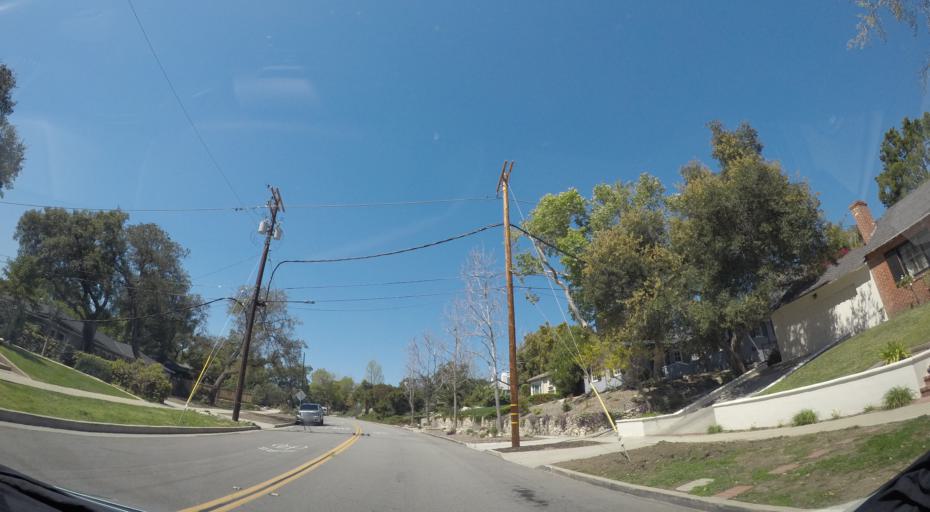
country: US
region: California
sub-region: Los Angeles County
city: Altadena
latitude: 34.1807
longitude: -118.1013
